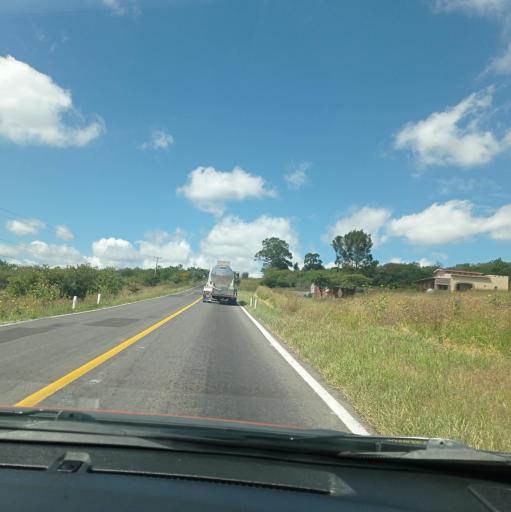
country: MX
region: Jalisco
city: Valle de Guadalupe
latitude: 21.0188
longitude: -102.5231
